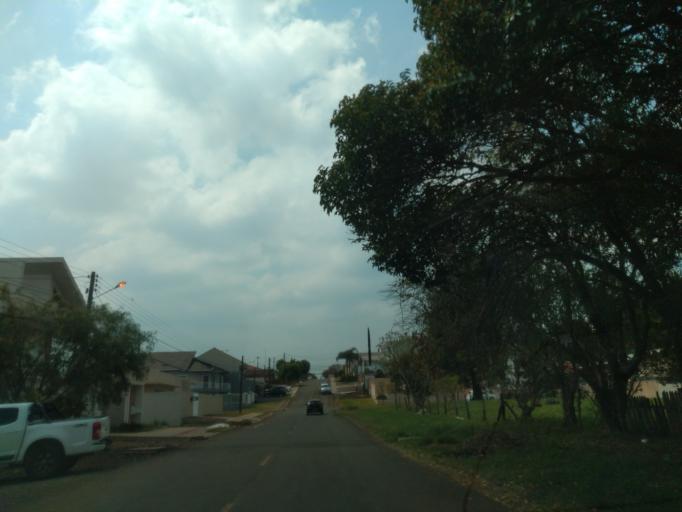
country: BR
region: Parana
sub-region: Guarapuava
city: Guarapuava
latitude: -25.3900
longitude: -51.4831
